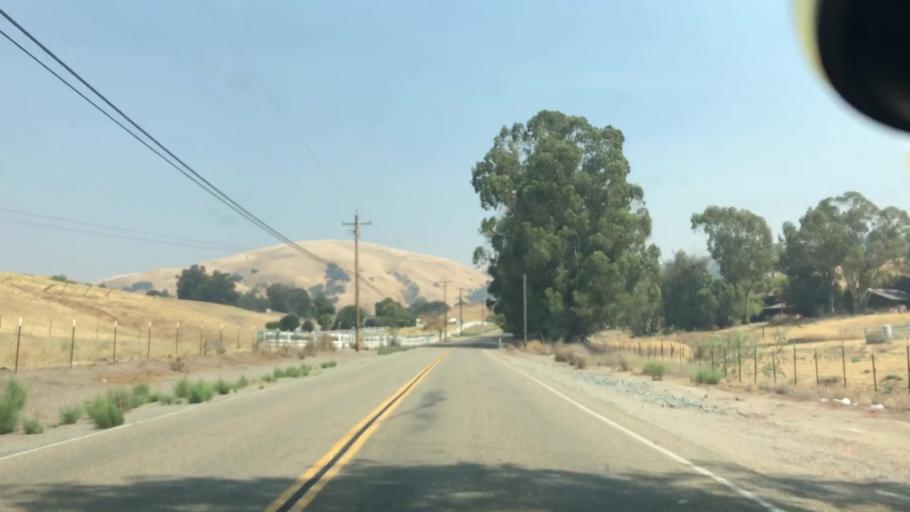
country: US
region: California
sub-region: Alameda County
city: Livermore
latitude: 37.6477
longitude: -121.6506
